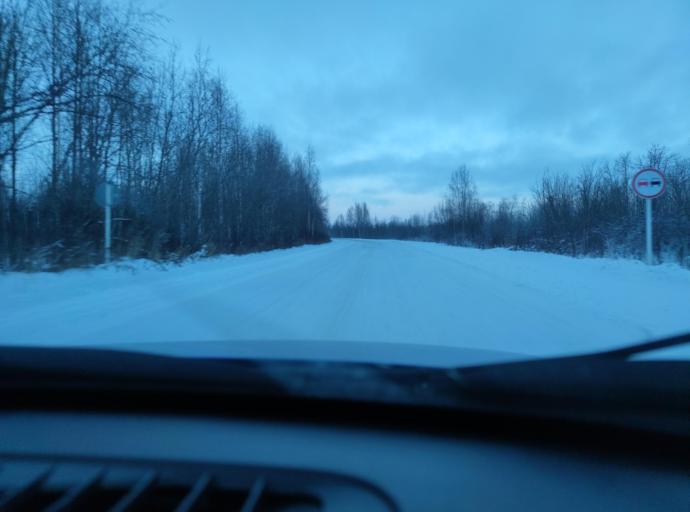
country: RU
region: Khanty-Mansiyskiy Avtonomnyy Okrug
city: Langepas
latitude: 61.1516
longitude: 75.1624
